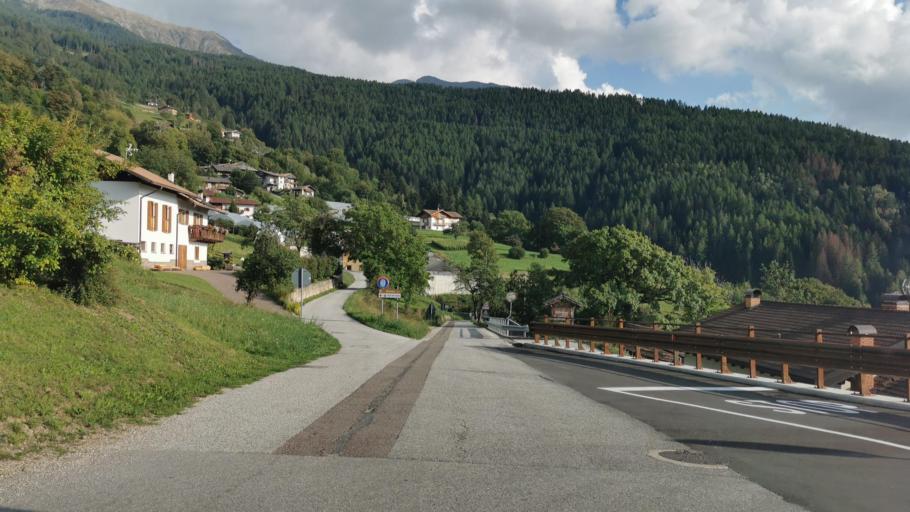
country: IT
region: Trentino-Alto Adige
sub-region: Provincia di Trento
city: Fierozzo
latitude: 46.1105
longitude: 11.3189
